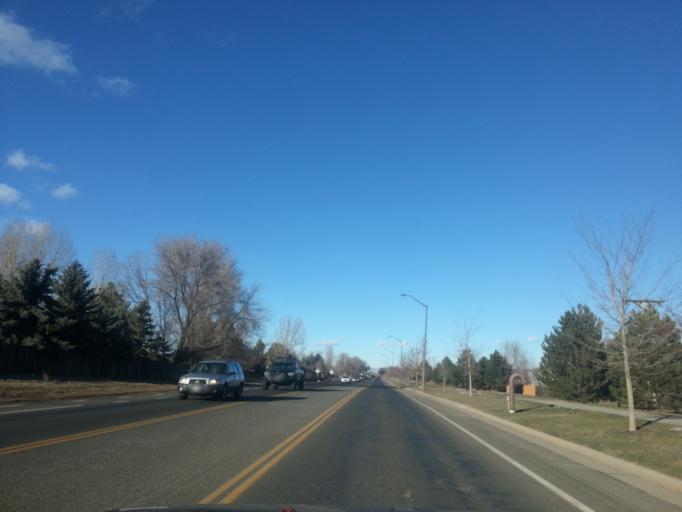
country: US
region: Colorado
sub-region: Larimer County
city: Fort Collins
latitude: 40.5263
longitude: -105.1150
